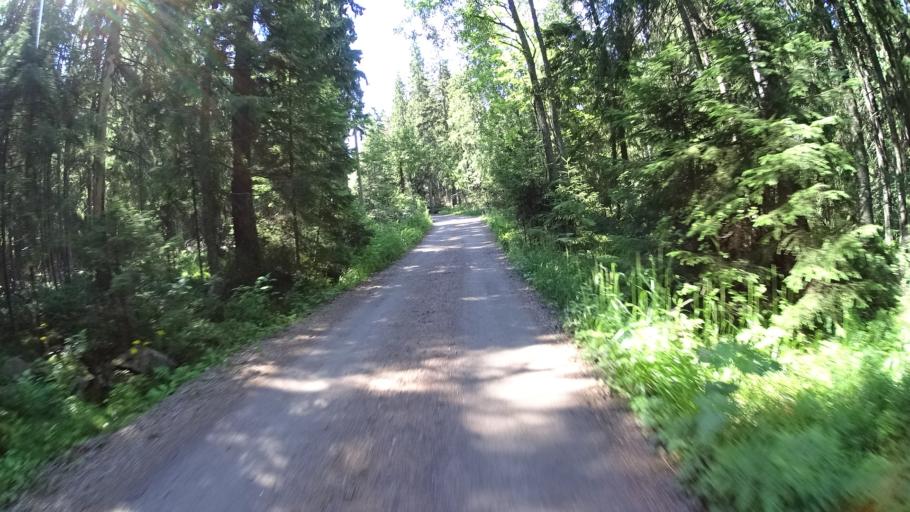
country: FI
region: Uusimaa
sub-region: Helsinki
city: Vihti
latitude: 60.3179
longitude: 24.4470
